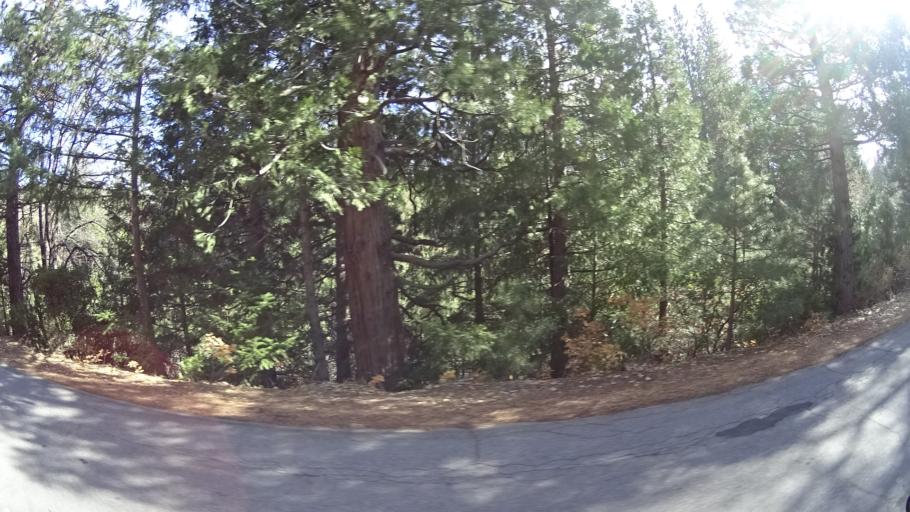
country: US
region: California
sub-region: Siskiyou County
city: Weed
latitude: 41.4286
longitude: -122.3985
